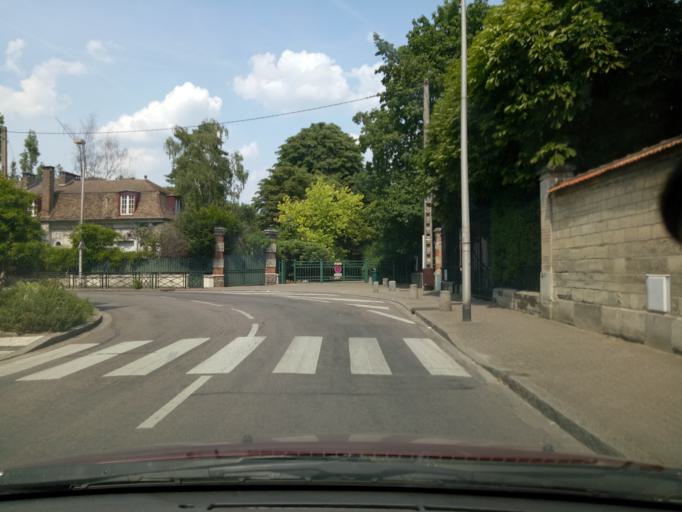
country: FR
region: Ile-de-France
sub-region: Departement des Yvelines
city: Chatou
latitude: 48.8910
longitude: 2.1601
